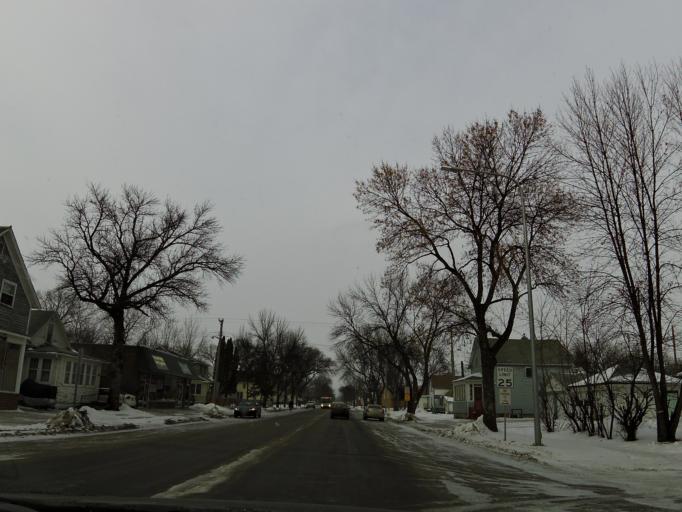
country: US
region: North Dakota
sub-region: Grand Forks County
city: Grand Forks
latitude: 47.9226
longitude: -97.0399
